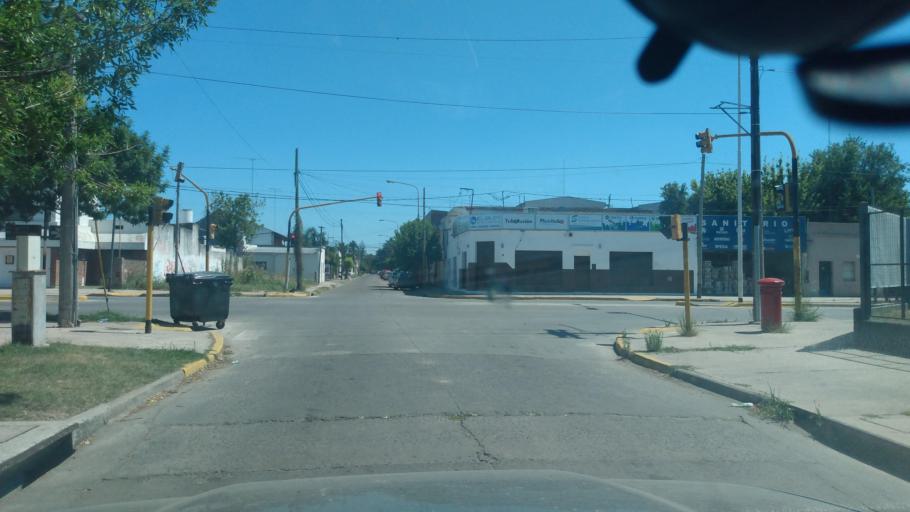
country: AR
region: Buenos Aires
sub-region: Partido de Lujan
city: Lujan
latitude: -34.5626
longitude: -59.1035
